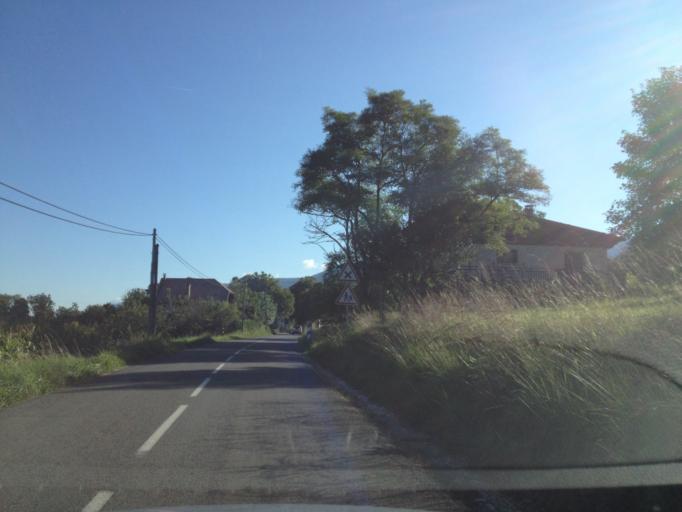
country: FR
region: Rhone-Alpes
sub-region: Departement de la Savoie
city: Gresy-sur-Aix
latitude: 45.7066
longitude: 5.9631
